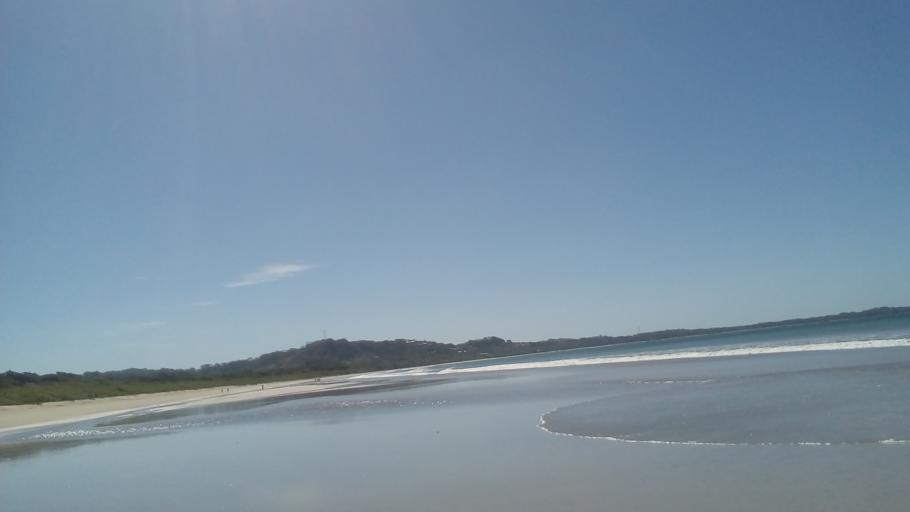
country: CR
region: Guanacaste
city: Santa Cruz
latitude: 10.3284
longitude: -85.8449
